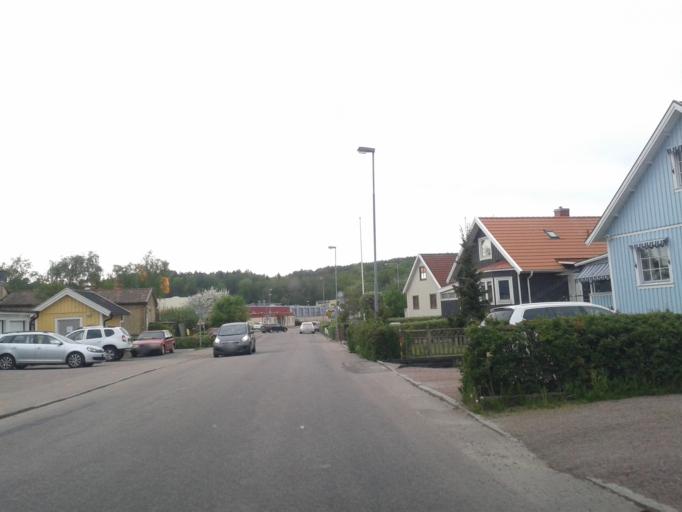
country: SE
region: Vaestra Goetaland
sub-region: Kungalvs Kommun
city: Kungalv
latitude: 57.8774
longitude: 11.9869
